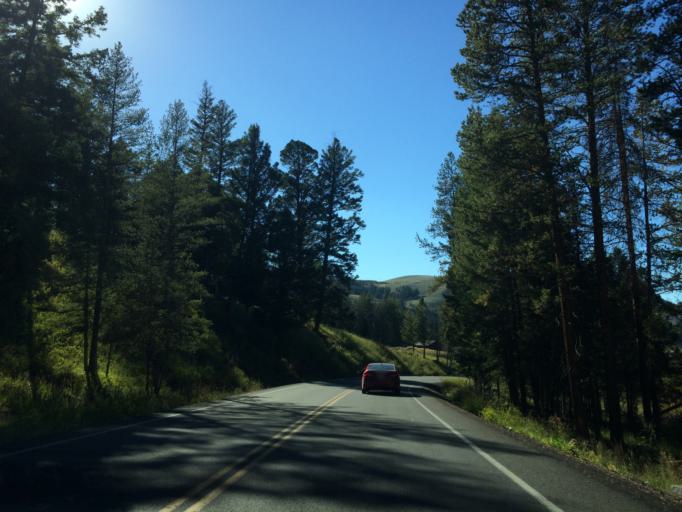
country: US
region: Montana
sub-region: Gallatin County
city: West Yellowstone
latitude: 44.9131
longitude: -110.4076
